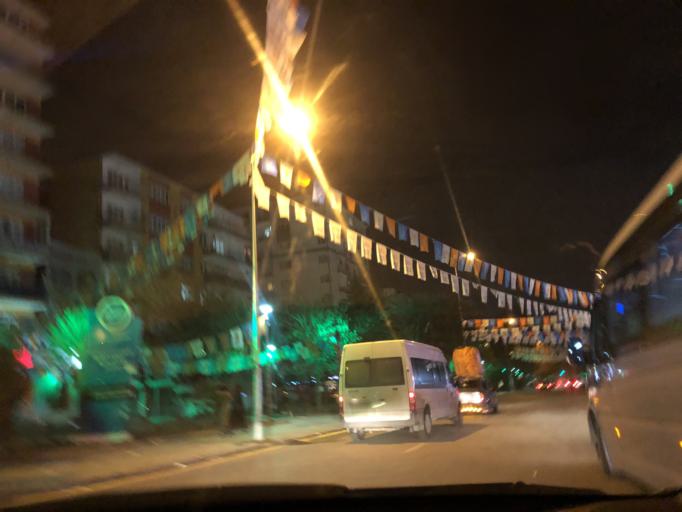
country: TR
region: Ankara
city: Batikent
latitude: 39.9689
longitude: 32.7846
